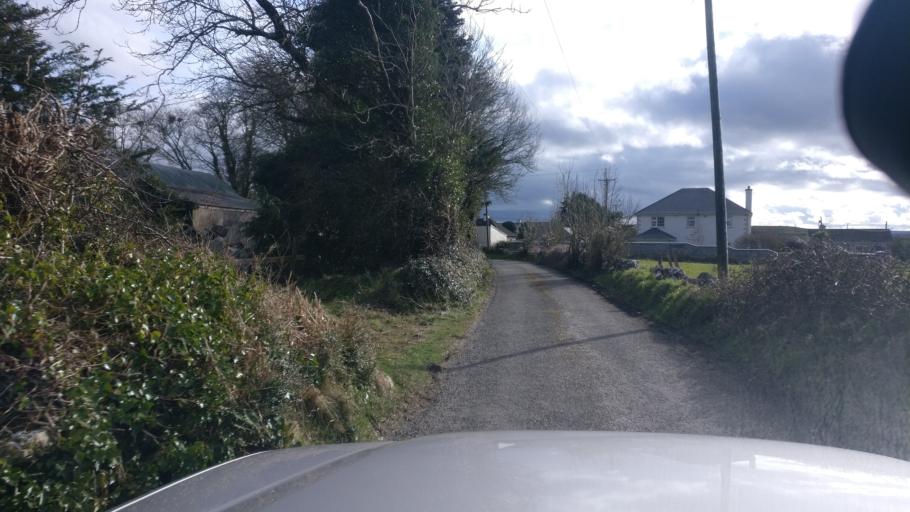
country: IE
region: Connaught
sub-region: County Galway
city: Loughrea
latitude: 53.1932
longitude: -8.5407
